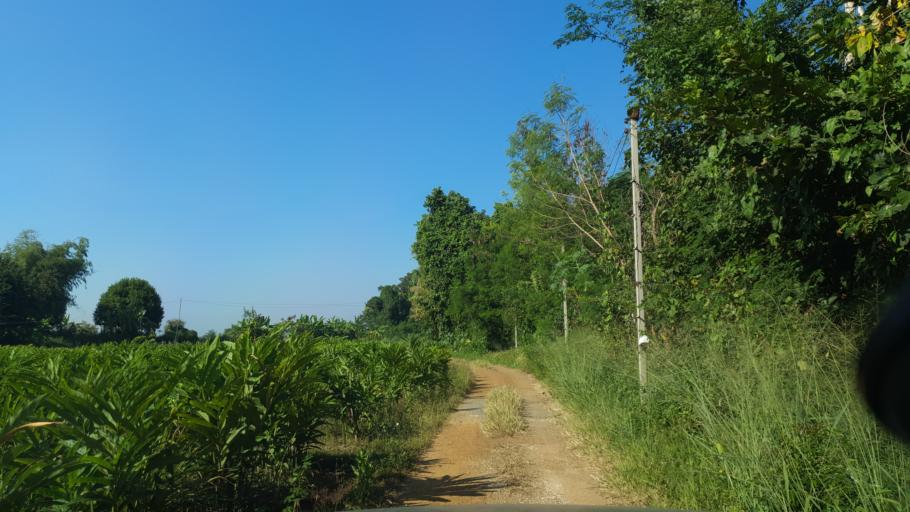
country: TH
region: Chiang Mai
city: San Kamphaeng
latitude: 18.7331
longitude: 99.1744
